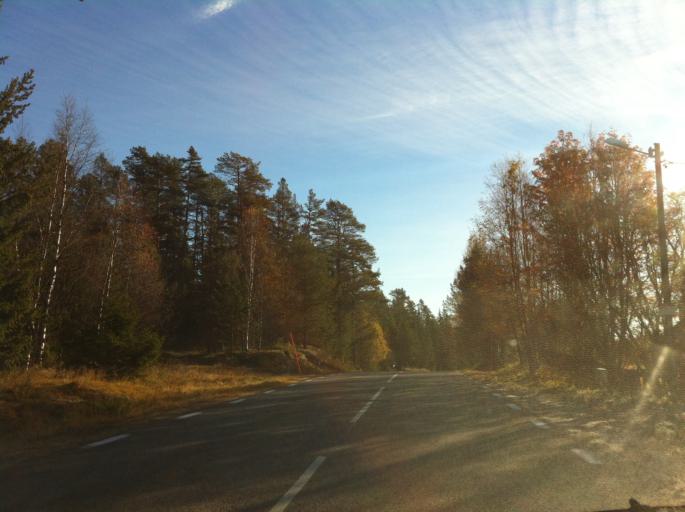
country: NO
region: Hedmark
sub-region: Engerdal
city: Engerdal
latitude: 62.0000
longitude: 12.4520
